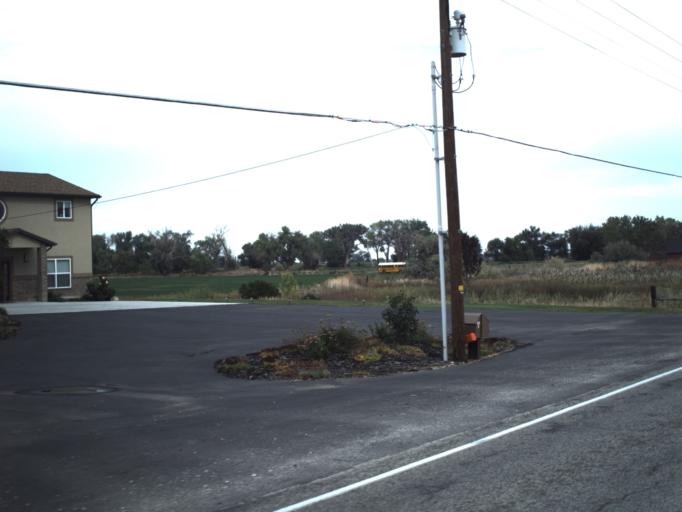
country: US
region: Utah
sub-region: Weber County
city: Plain City
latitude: 41.2721
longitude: -112.0923
